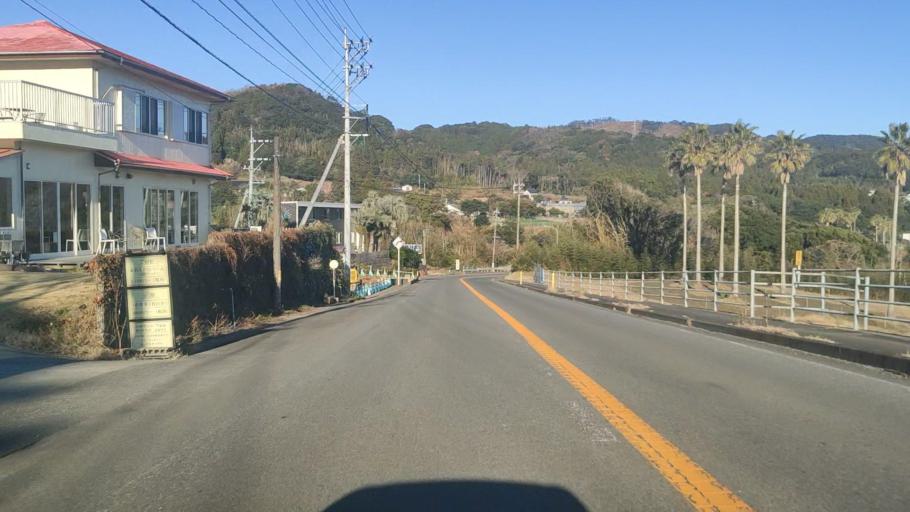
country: JP
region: Miyazaki
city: Nobeoka
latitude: 32.3530
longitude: 131.6226
